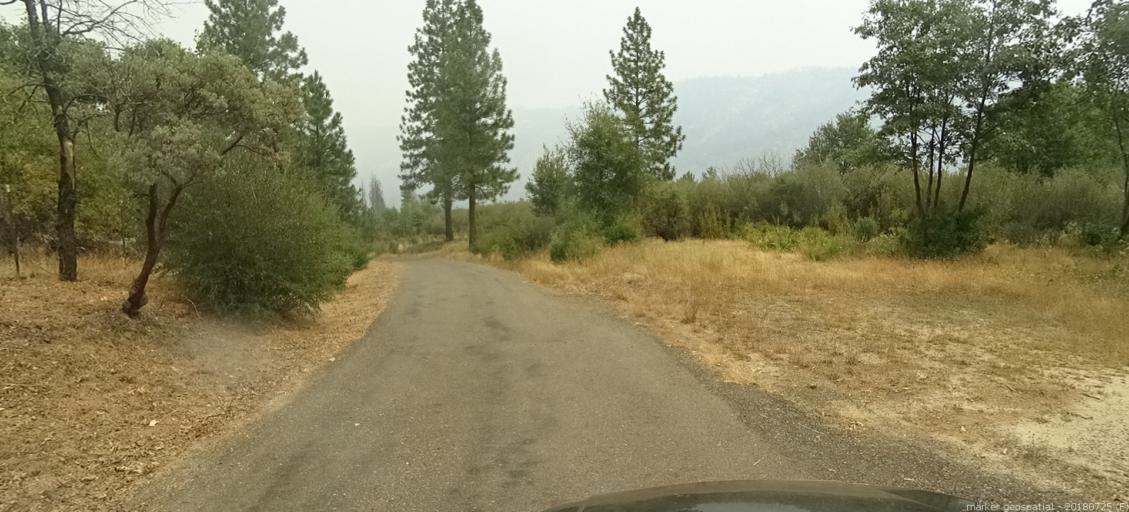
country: US
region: California
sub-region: Madera County
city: Oakhurst
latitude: 37.2649
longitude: -119.5083
